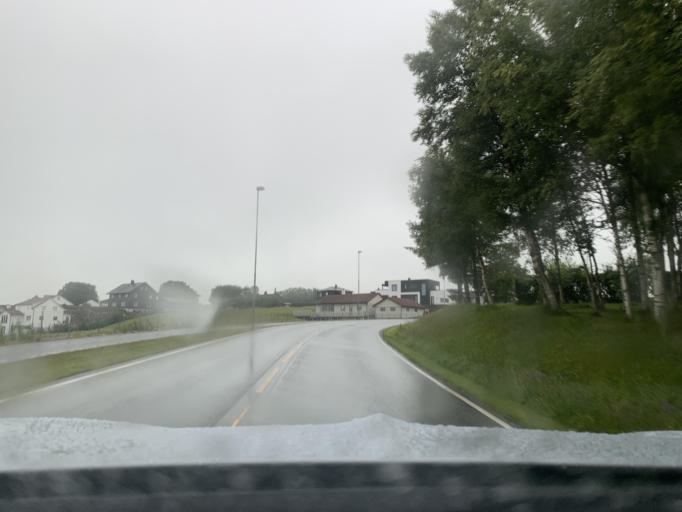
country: NO
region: Rogaland
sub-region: Time
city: Bryne
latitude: 58.7374
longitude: 5.6359
